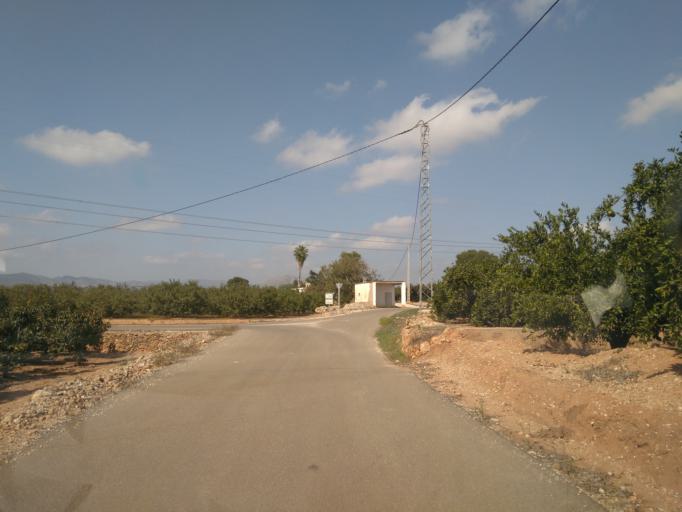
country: ES
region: Valencia
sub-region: Provincia de Valencia
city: Benimodo
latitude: 39.1809
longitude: -0.5496
